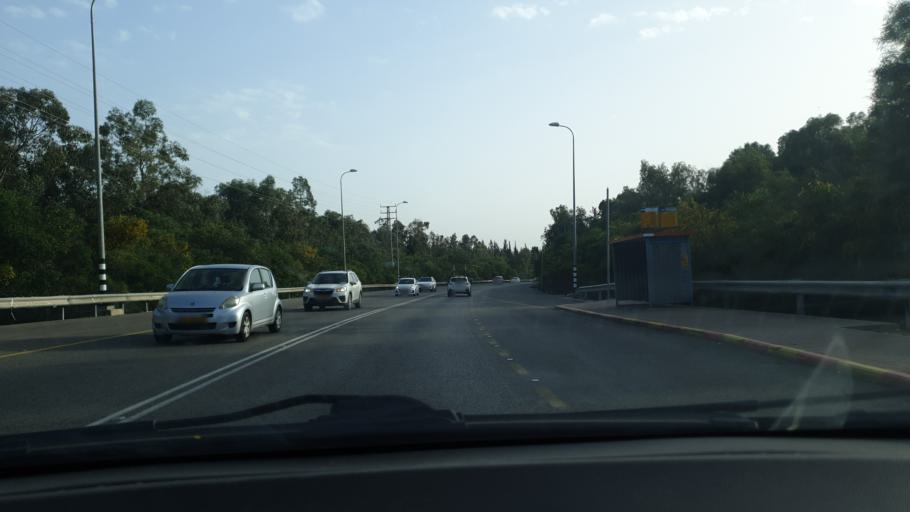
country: IL
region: Central District
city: Tel Mond
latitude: 32.2718
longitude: 34.9225
